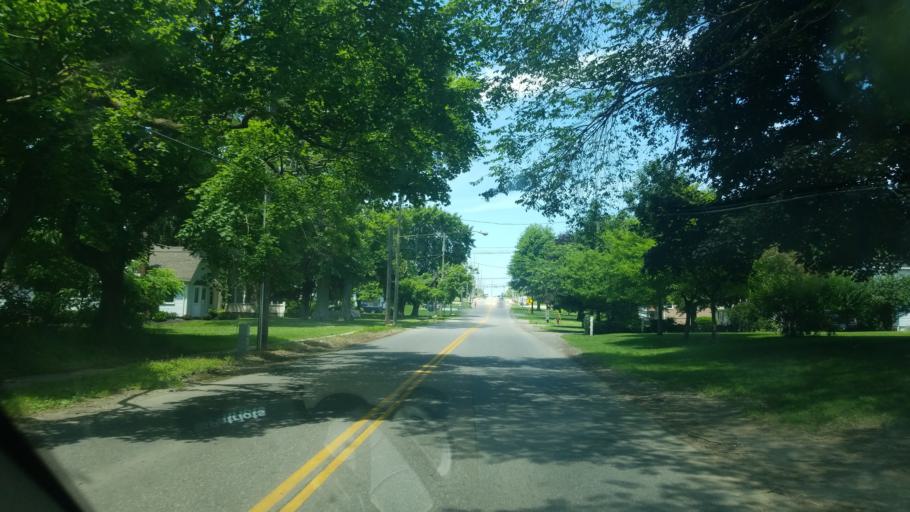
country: US
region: Ohio
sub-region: Columbiana County
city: Lisbon
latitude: 40.7822
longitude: -80.7717
